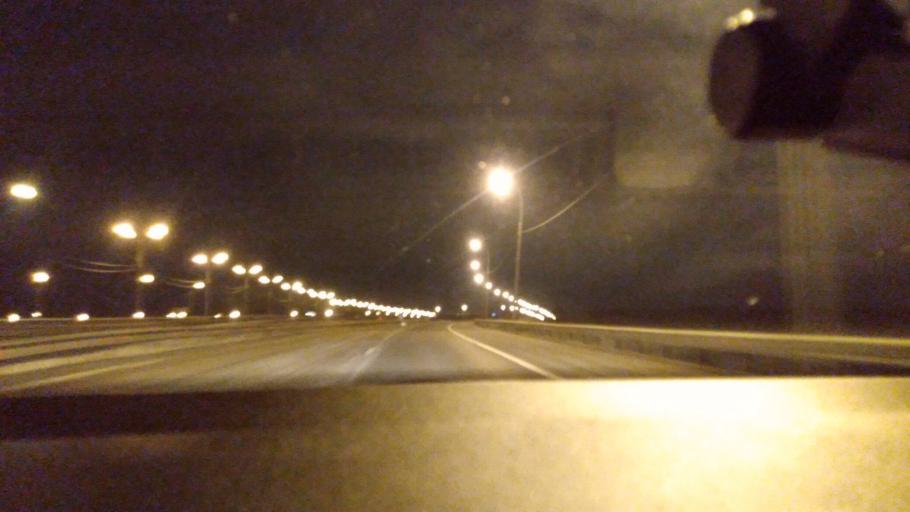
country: RU
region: Moskovskaya
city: Raduzhnyy
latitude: 55.1539
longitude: 38.6975
